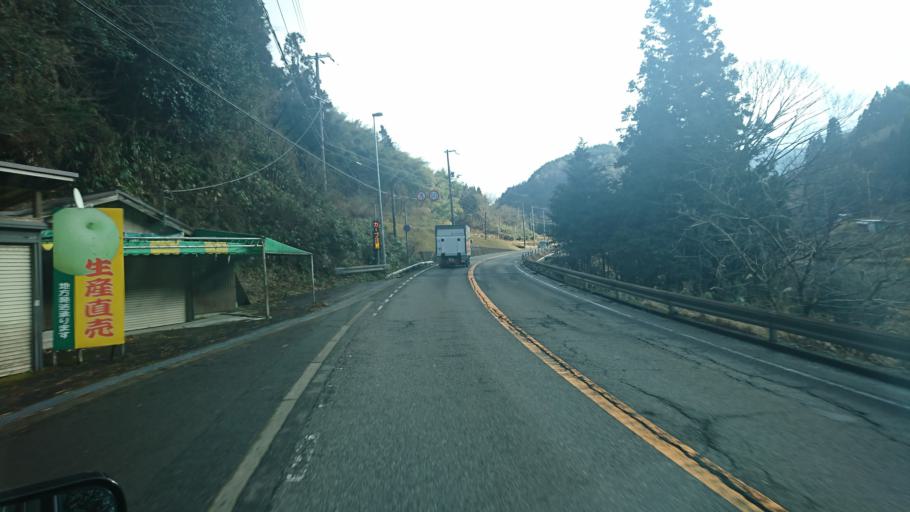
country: JP
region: Tottori
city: Tottori
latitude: 35.5390
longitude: 134.5102
